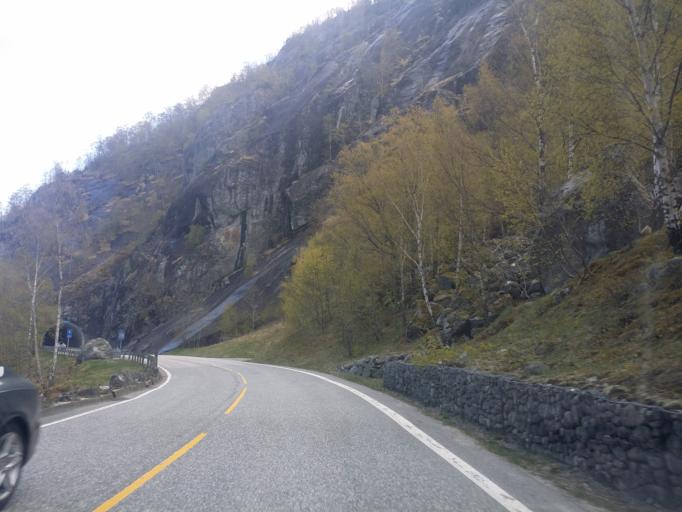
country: NO
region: Hordaland
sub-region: Eidfjord
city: Eidfjord
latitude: 60.4533
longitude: 7.0917
